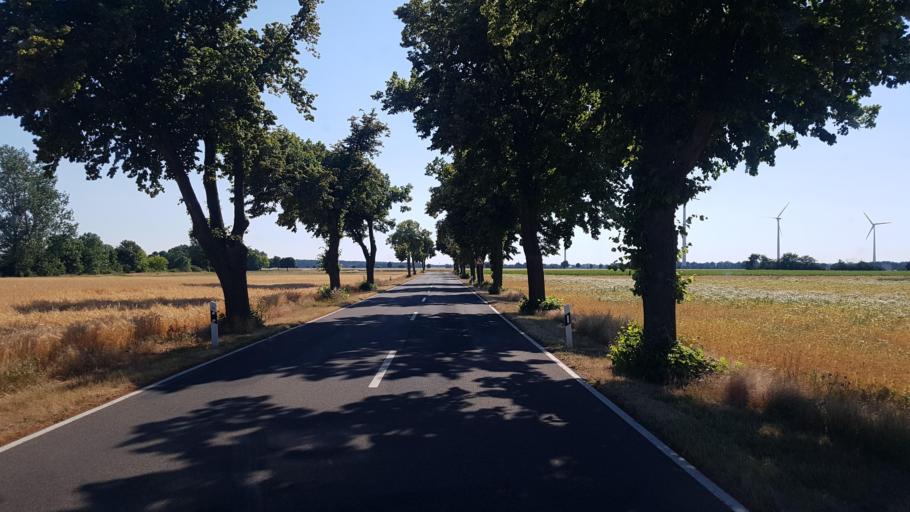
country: DE
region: Saxony-Anhalt
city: Prettin
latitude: 51.6780
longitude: 12.9714
